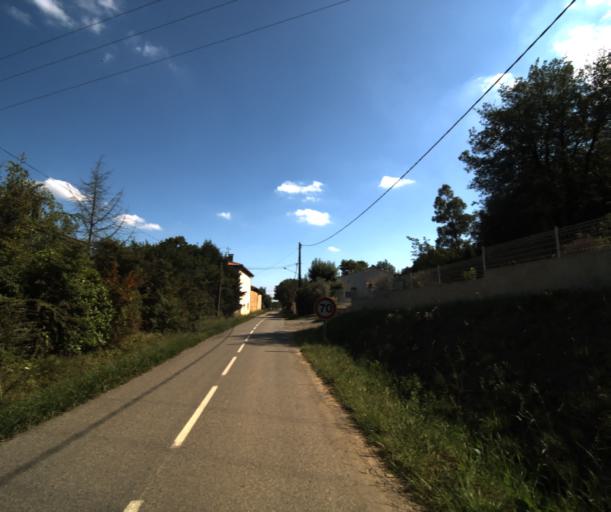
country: FR
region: Midi-Pyrenees
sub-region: Departement de la Haute-Garonne
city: Fonsorbes
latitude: 43.5071
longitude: 1.2196
